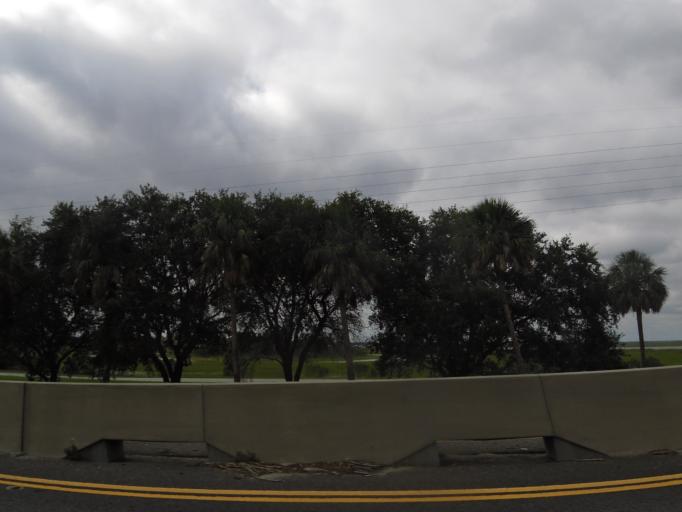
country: US
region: Georgia
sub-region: Glynn County
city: Saint Simon Mills
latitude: 31.1634
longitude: -81.4491
